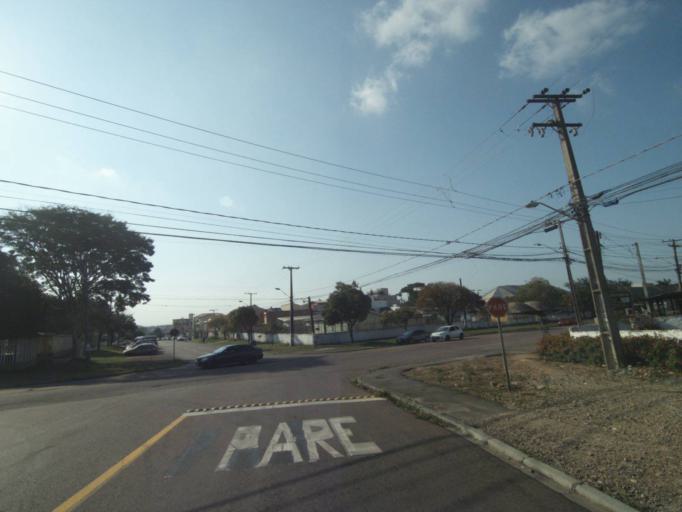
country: BR
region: Parana
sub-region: Curitiba
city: Curitiba
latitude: -25.4860
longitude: -49.3249
